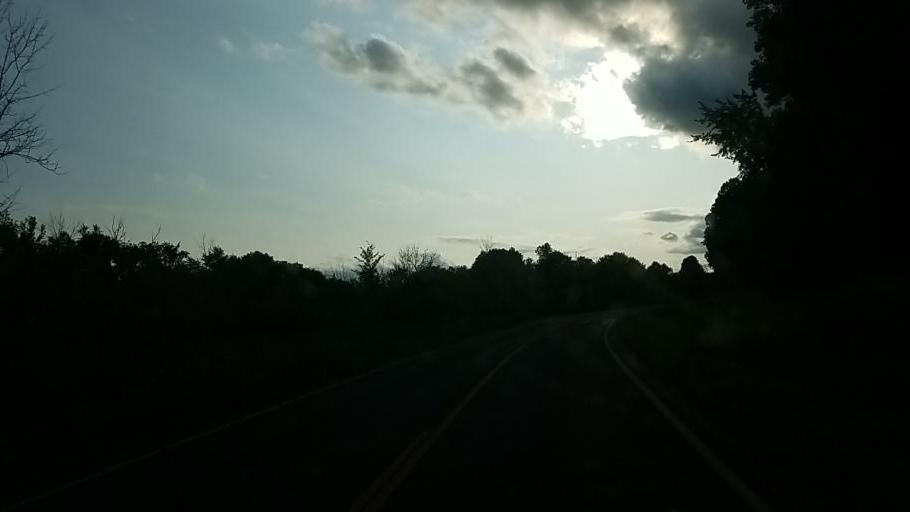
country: US
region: Michigan
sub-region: Montcalm County
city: Howard City
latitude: 43.3087
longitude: -85.3722
